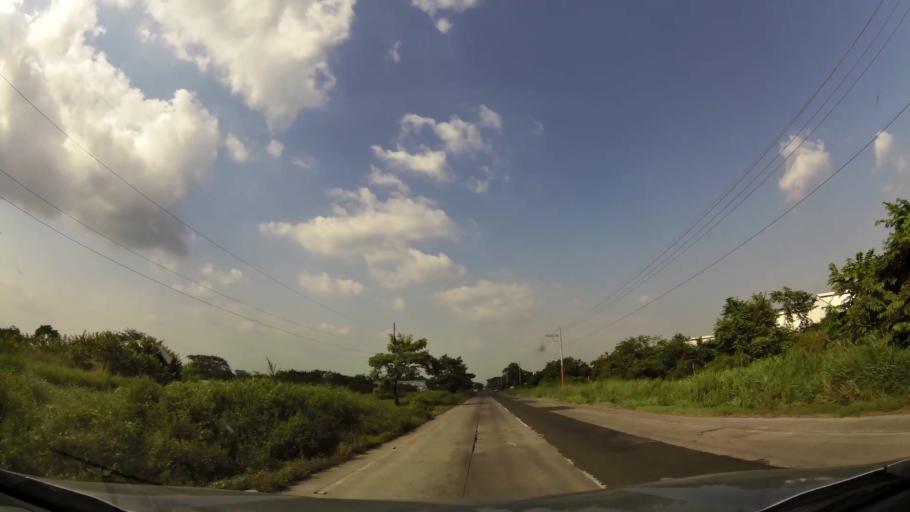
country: GT
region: Escuintla
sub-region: Municipio de Masagua
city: Masagua
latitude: 14.0975
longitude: -90.7796
